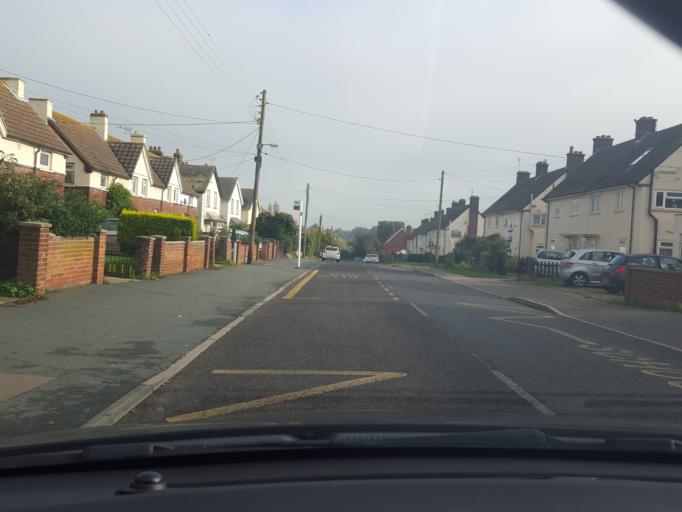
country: GB
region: England
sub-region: Essex
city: Manningtree
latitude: 51.9411
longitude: 1.0548
